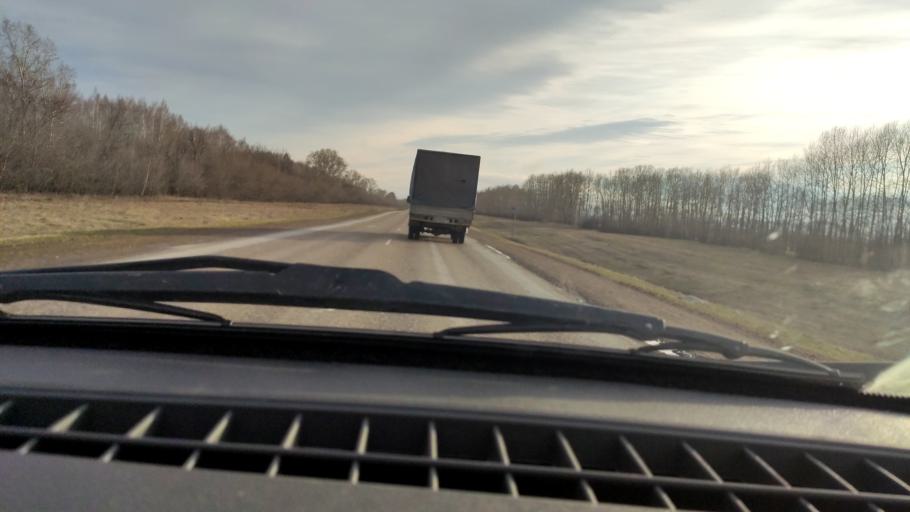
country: RU
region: Bashkortostan
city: Davlekanovo
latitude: 54.3589
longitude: 55.1909
